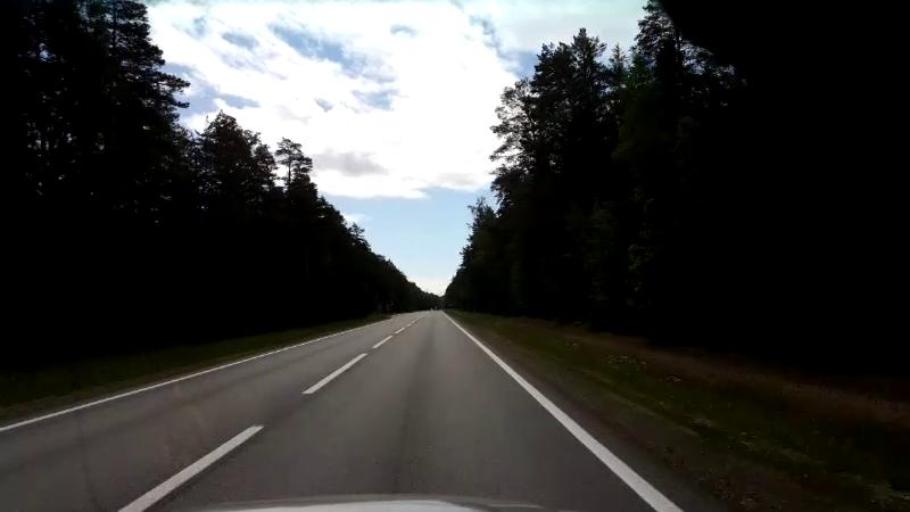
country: LV
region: Saulkrastu
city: Saulkrasti
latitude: 57.5116
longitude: 24.4306
